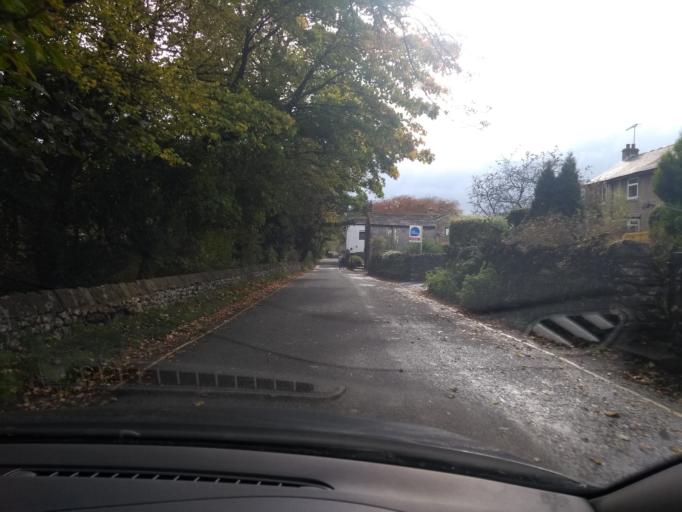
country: GB
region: England
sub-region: North Yorkshire
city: Gargrave
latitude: 54.0628
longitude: -2.1536
